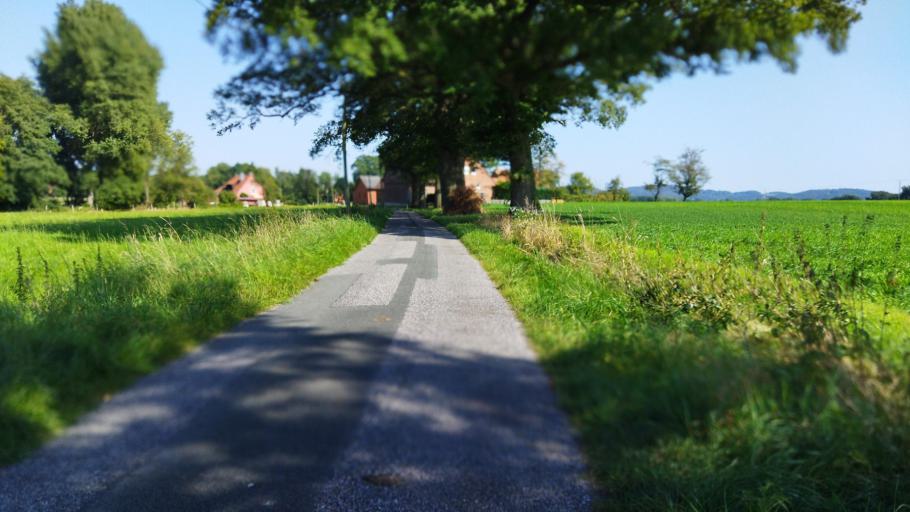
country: DE
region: Lower Saxony
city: Hasbergen
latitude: 52.2288
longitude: 7.9035
